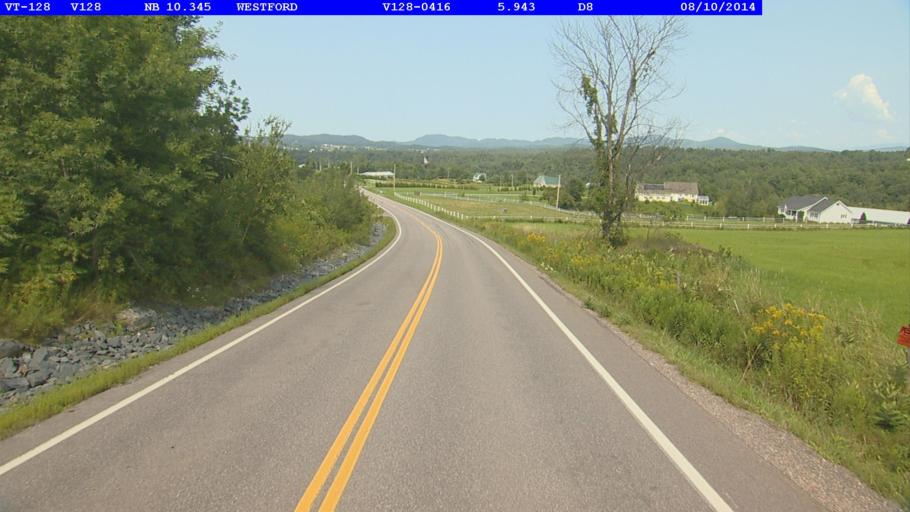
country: US
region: Vermont
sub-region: Chittenden County
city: Milton
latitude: 44.6387
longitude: -73.0164
